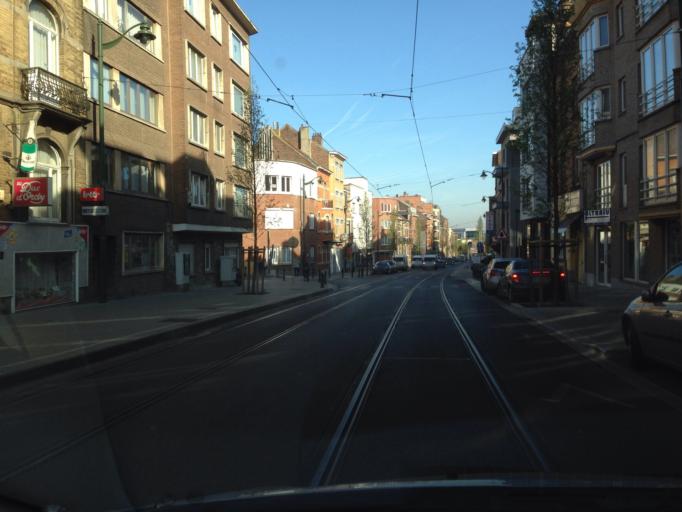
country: BE
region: Flanders
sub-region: Provincie Vlaams-Brabant
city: Dilbeek
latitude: 50.8669
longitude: 4.2946
